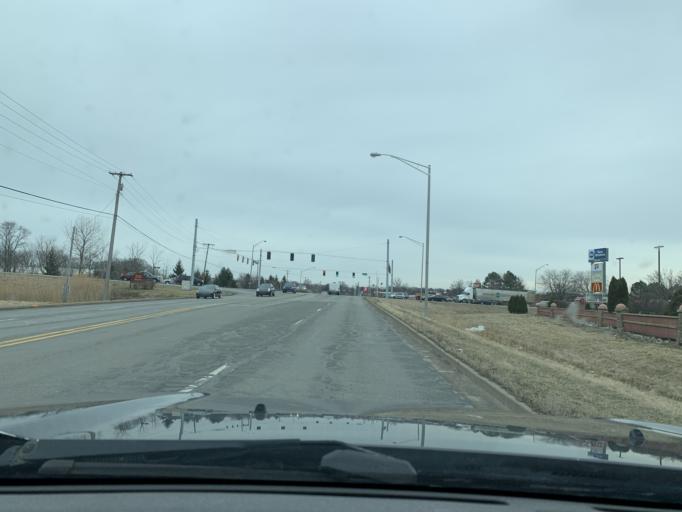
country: US
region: Indiana
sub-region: Porter County
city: Chesterton
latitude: 41.6168
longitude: -87.0429
